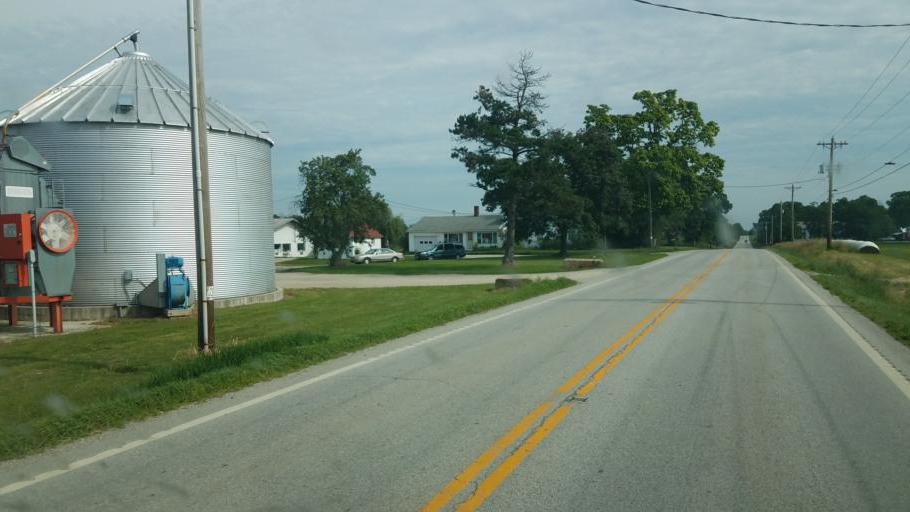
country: US
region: Ohio
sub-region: Medina County
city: Lodi
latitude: 41.1448
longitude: -82.0234
